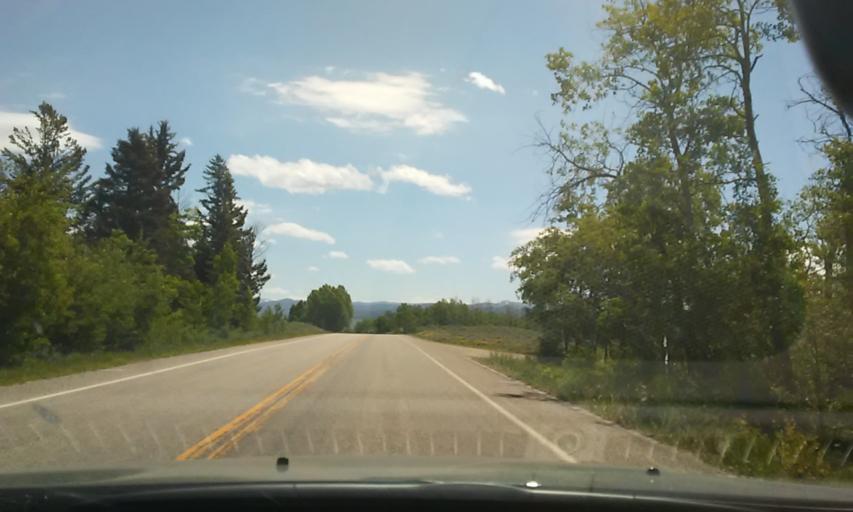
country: US
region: Wyoming
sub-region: Teton County
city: Jackson
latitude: 43.8388
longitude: -110.4854
